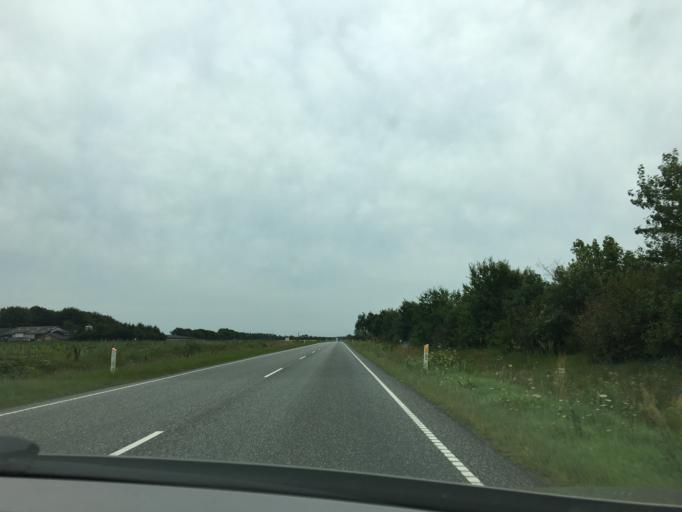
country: DK
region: Central Jutland
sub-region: Herning Kommune
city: Sunds
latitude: 56.2371
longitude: 9.0078
